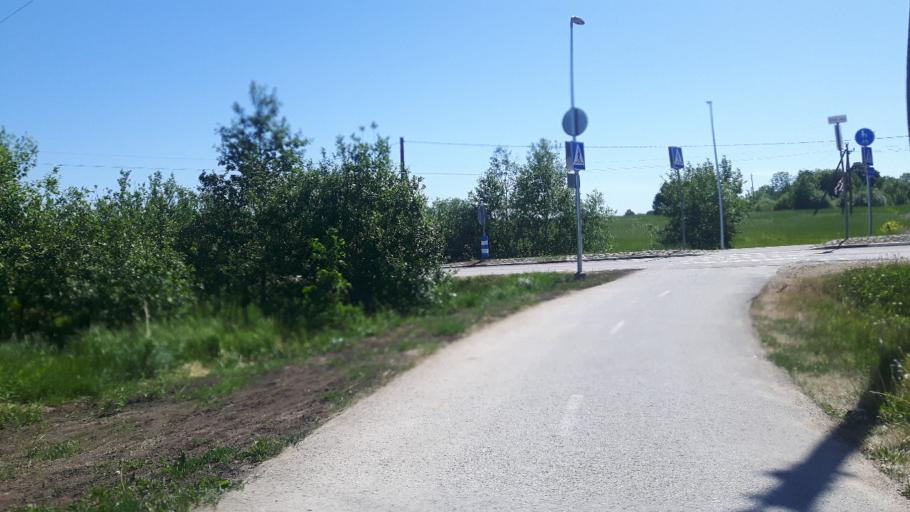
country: EE
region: Harju
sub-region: Saku vald
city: Saku
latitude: 59.2893
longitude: 24.6614
